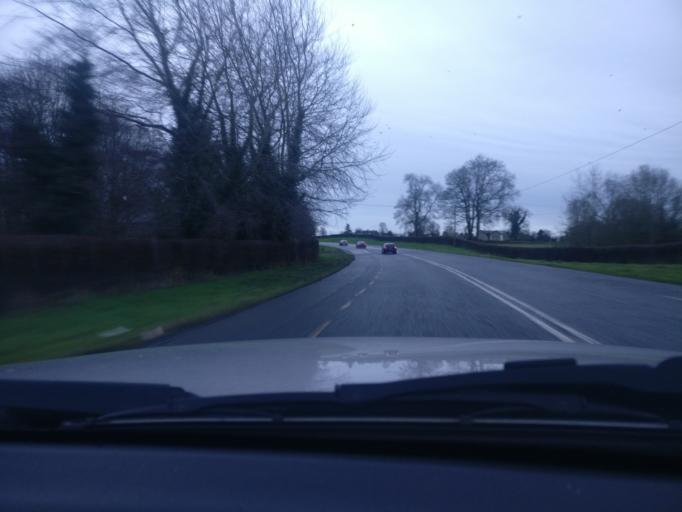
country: IE
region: Leinster
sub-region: An Mhi
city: Kells
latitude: 53.6945
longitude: -6.7875
